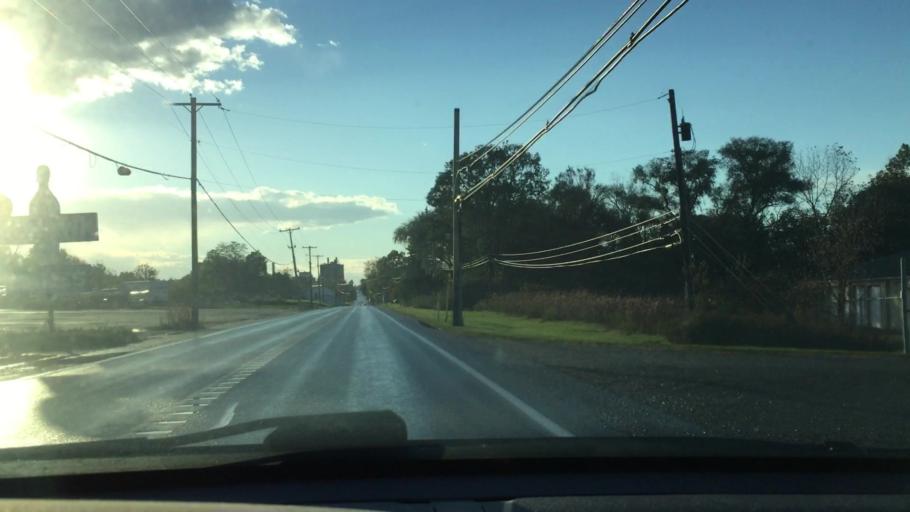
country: US
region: Pennsylvania
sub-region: Lawrence County
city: Bessemer
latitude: 40.9759
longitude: -80.4703
